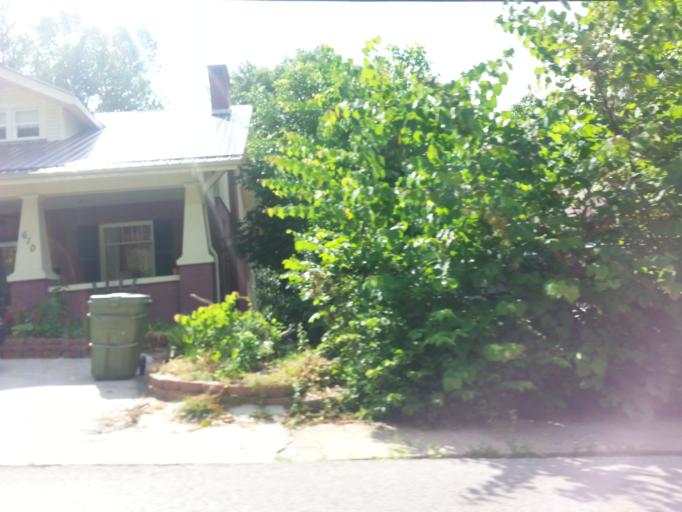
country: US
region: Kentucky
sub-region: Harlan County
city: Harlan
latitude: 36.8400
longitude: -83.3242
